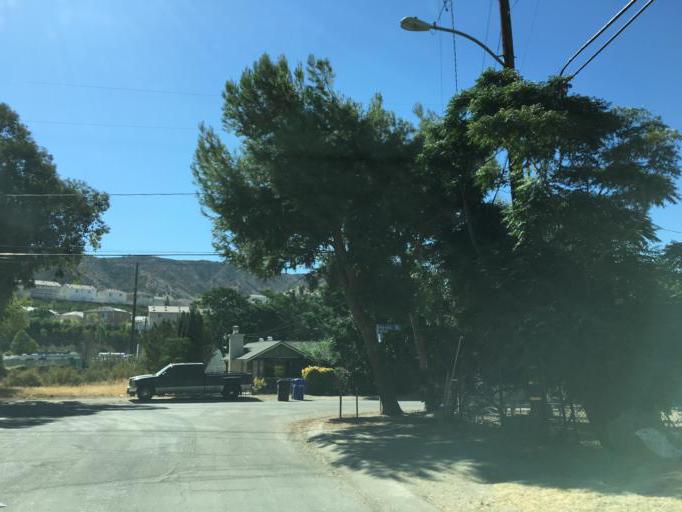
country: US
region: California
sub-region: Los Angeles County
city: Agua Dulce
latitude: 34.4455
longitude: -118.4292
